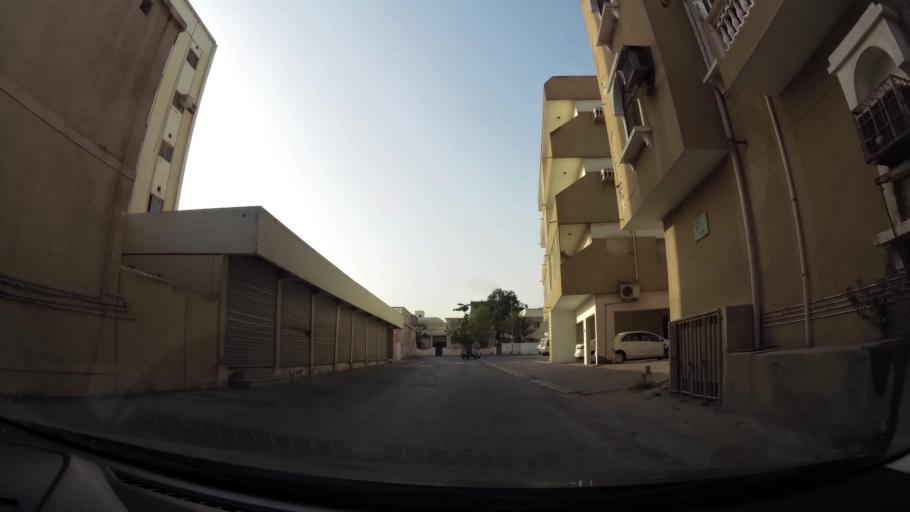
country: OM
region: Zufar
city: Salalah
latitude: 17.0087
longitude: 54.0847
